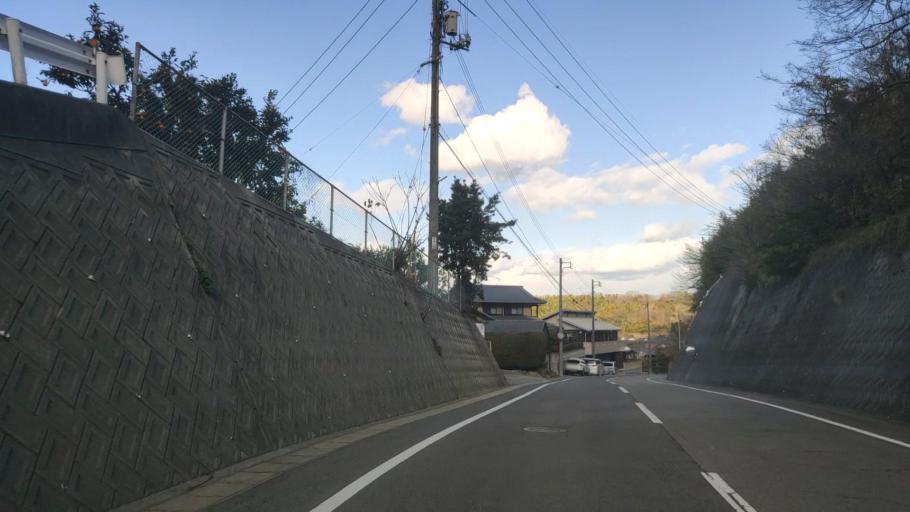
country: JP
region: Hiroshima
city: Innoshima
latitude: 34.2089
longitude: 133.1220
